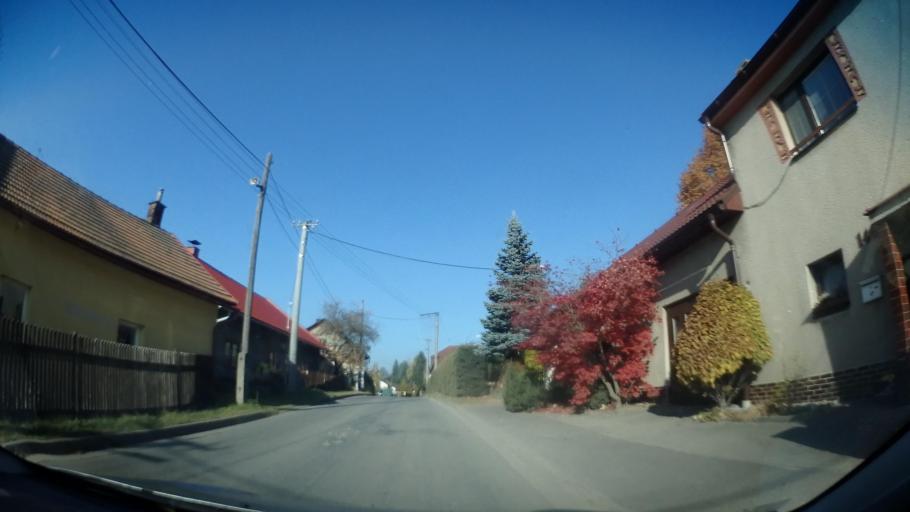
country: CZ
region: Vysocina
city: Zd'ar nad Sazavou Druhy
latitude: 49.6048
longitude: 15.9230
